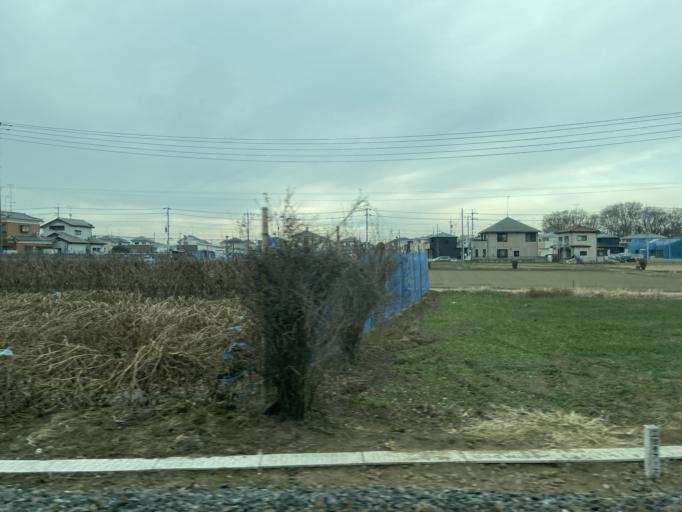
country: JP
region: Ibaraki
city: Koga
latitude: 36.1705
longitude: 139.7167
